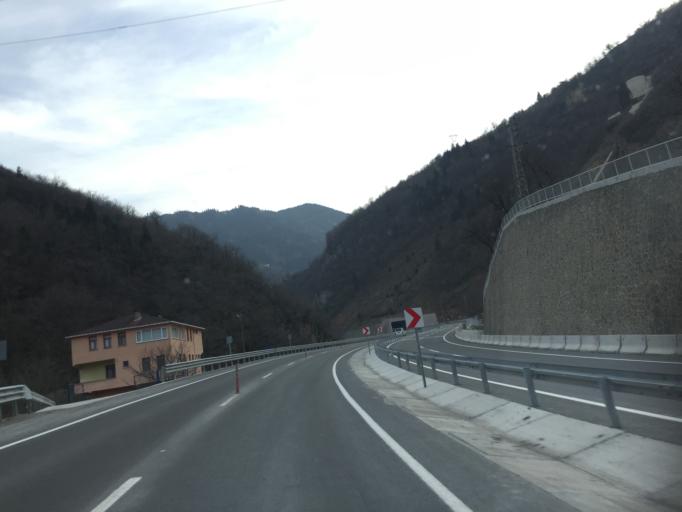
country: TR
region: Trabzon
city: Macka
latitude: 40.7605
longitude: 39.5635
